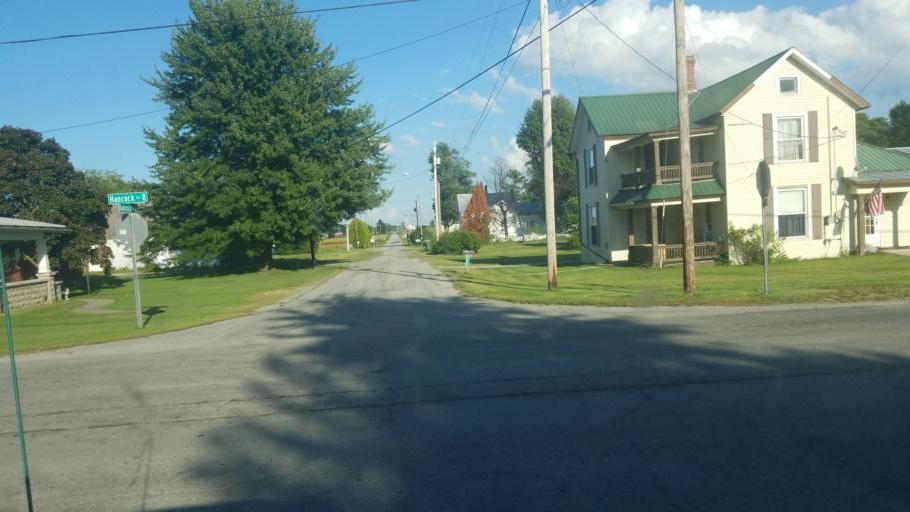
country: US
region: Ohio
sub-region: Hancock County
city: Arlington
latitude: 40.9354
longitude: -83.5945
